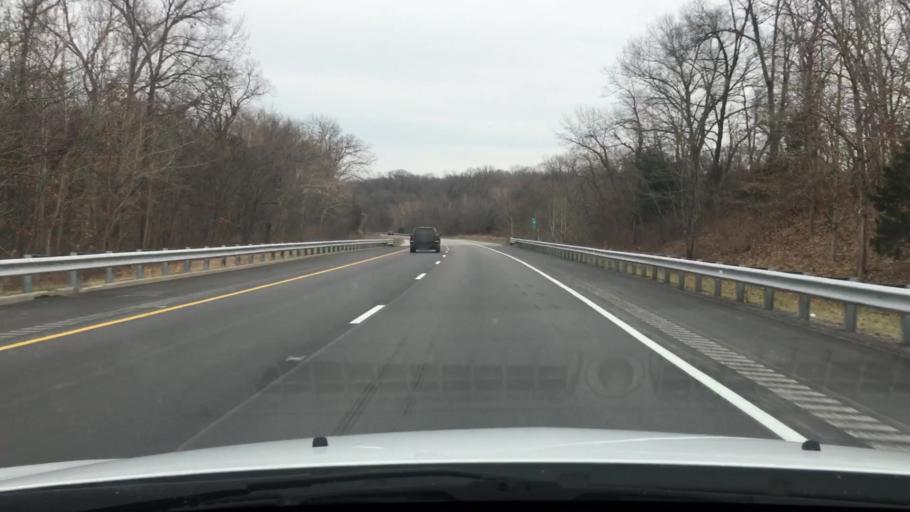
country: US
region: Illinois
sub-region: Pike County
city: Griggsville
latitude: 39.6811
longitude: -90.6587
